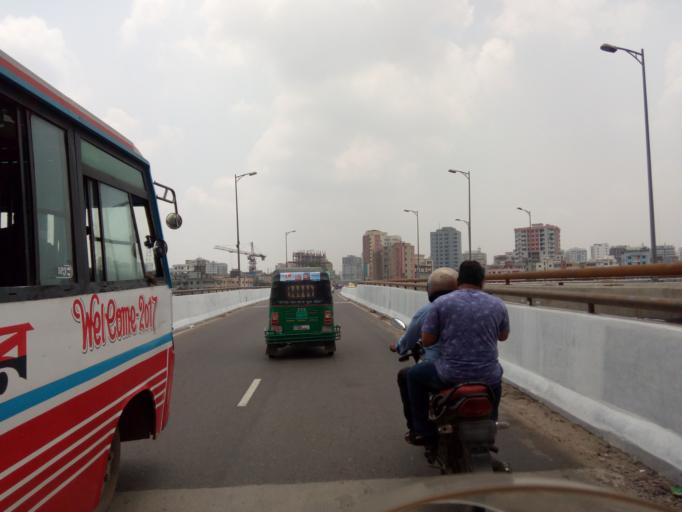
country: BD
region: Dhaka
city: Paltan
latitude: 23.7538
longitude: 90.4006
